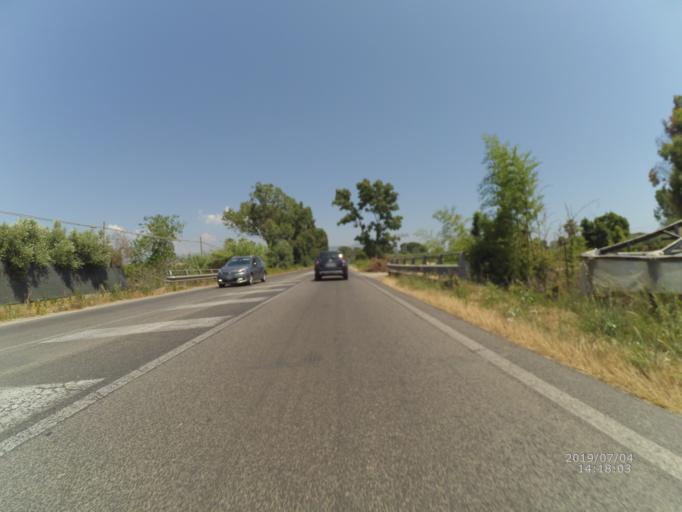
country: IT
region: Latium
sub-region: Provincia di Latina
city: Monte San Biagio
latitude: 41.2891
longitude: 13.3701
